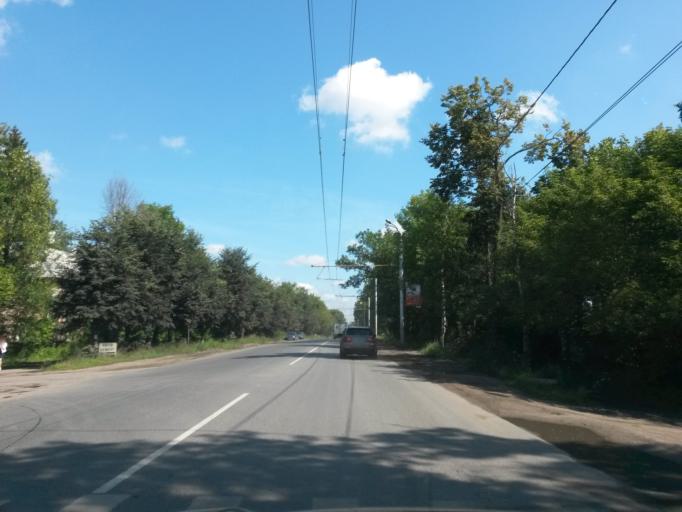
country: RU
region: Ivanovo
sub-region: Gorod Ivanovo
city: Ivanovo
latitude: 57.0037
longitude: 40.9458
